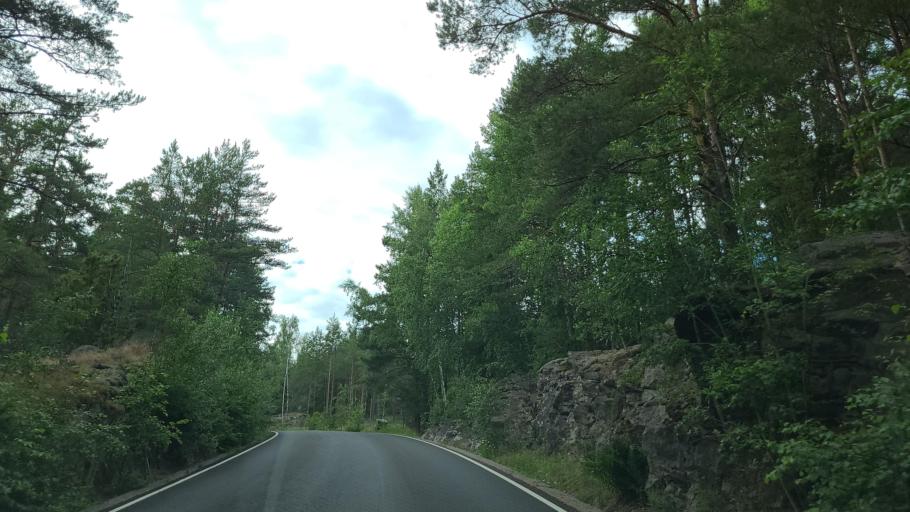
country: FI
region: Varsinais-Suomi
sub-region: Turku
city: Rymaettylae
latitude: 60.3180
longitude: 21.9630
